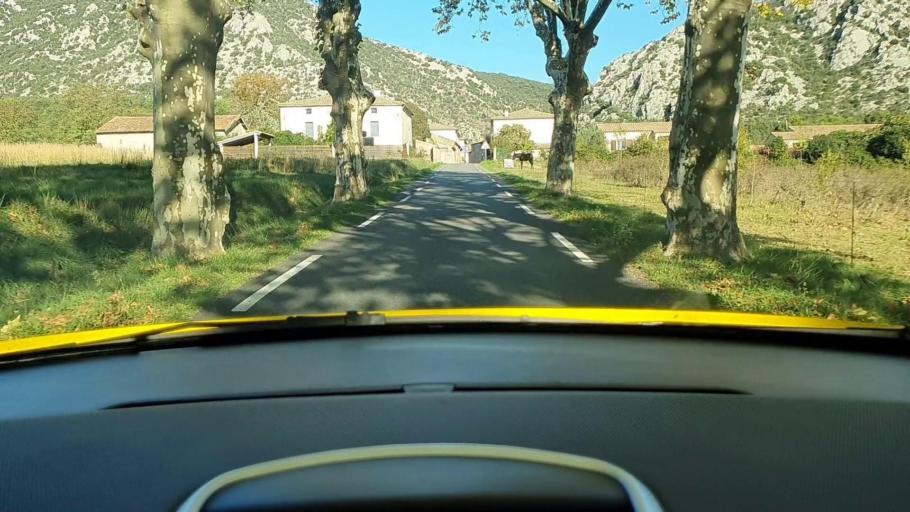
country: FR
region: Languedoc-Roussillon
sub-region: Departement du Gard
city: Saint-Hippolyte-du-Fort
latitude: 43.9552
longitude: 3.8089
